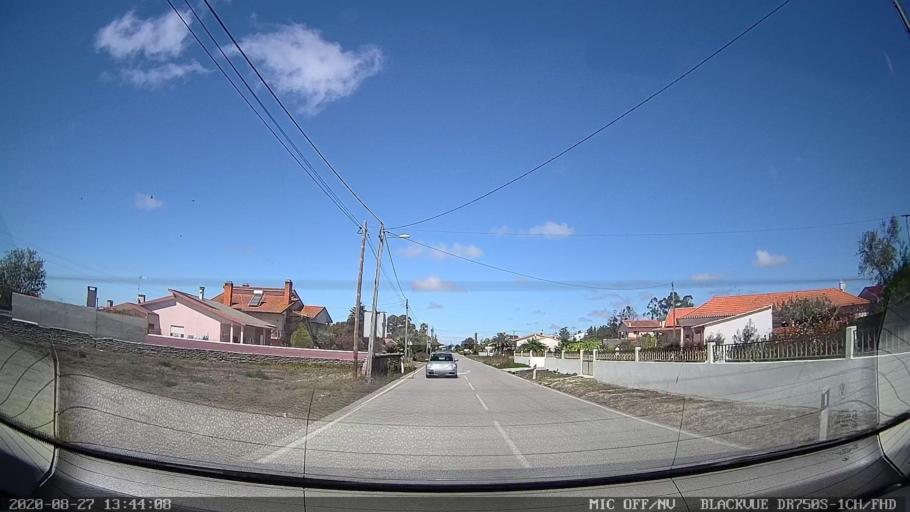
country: PT
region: Coimbra
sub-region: Mira
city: Mira
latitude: 40.4150
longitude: -8.7359
